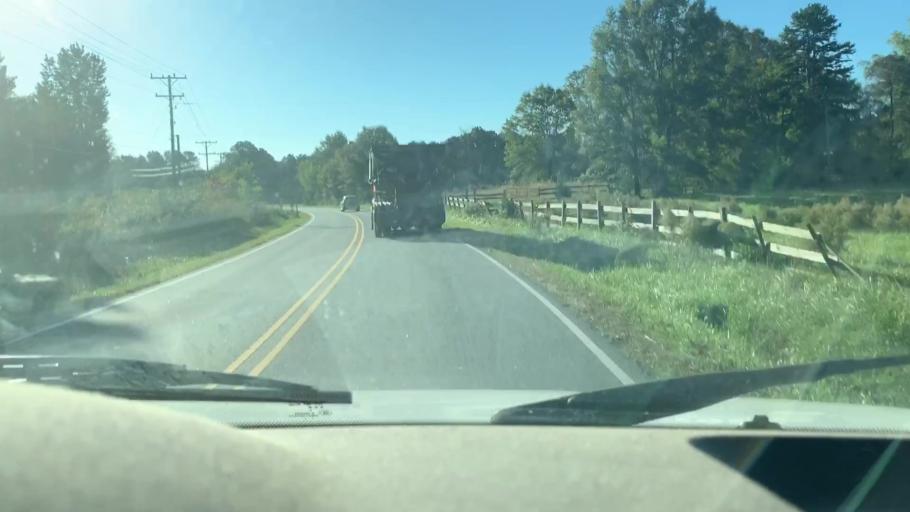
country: US
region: North Carolina
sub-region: Mecklenburg County
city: Huntersville
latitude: 35.4321
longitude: -80.7625
